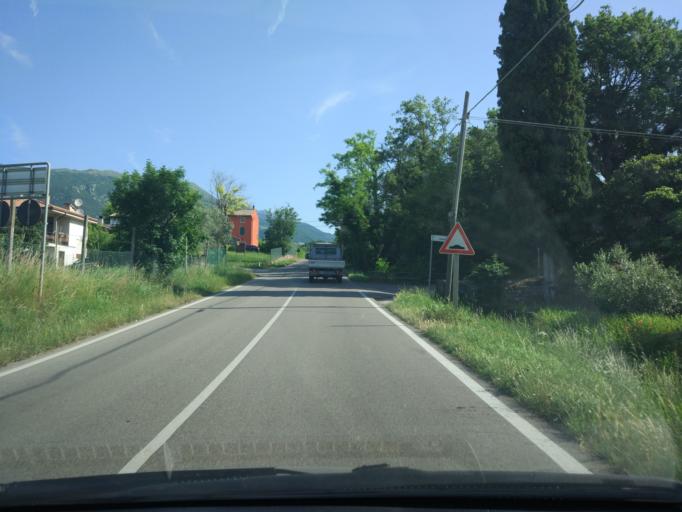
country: IT
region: Veneto
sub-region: Provincia di Verona
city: Rivoli Veronese
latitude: 45.5863
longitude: 10.8121
